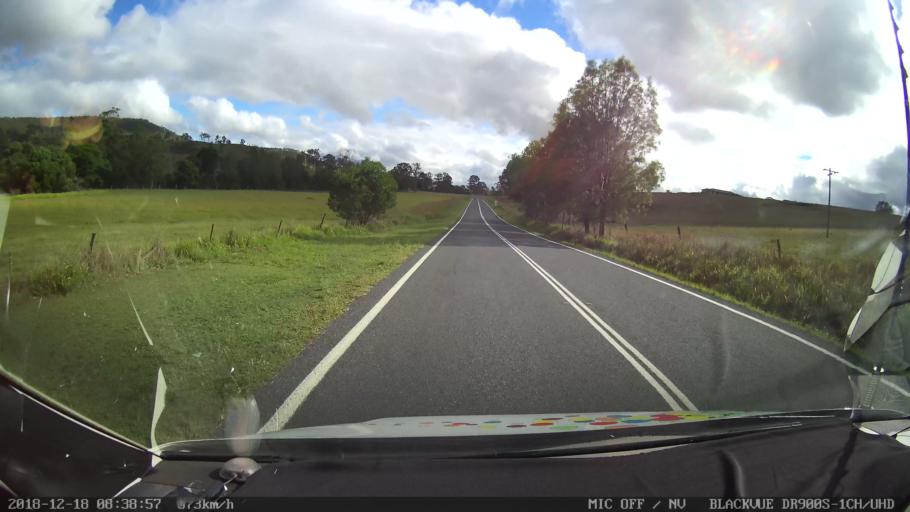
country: AU
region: New South Wales
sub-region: Kyogle
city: Kyogle
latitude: -28.2523
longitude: 152.8332
